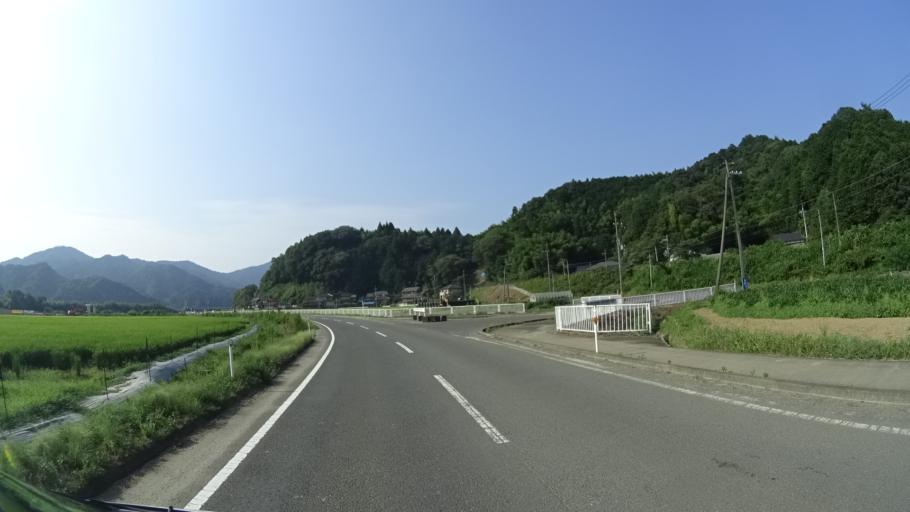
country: JP
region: Kyoto
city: Maizuru
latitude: 35.4617
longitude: 135.2871
